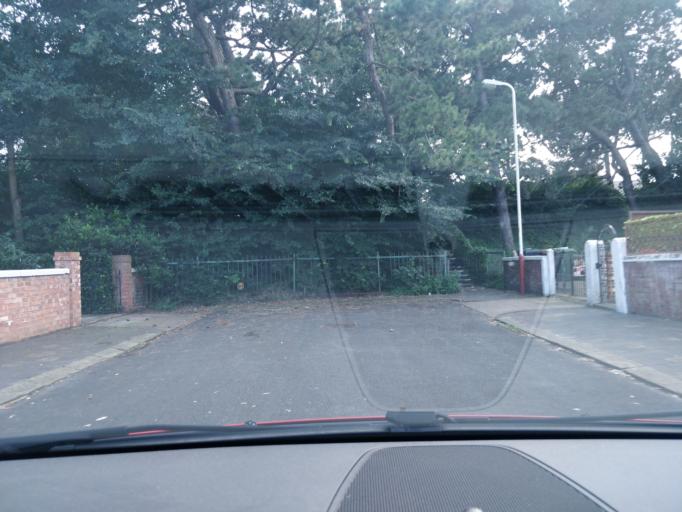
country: GB
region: England
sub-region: Sefton
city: Southport
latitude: 53.6465
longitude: -2.9837
